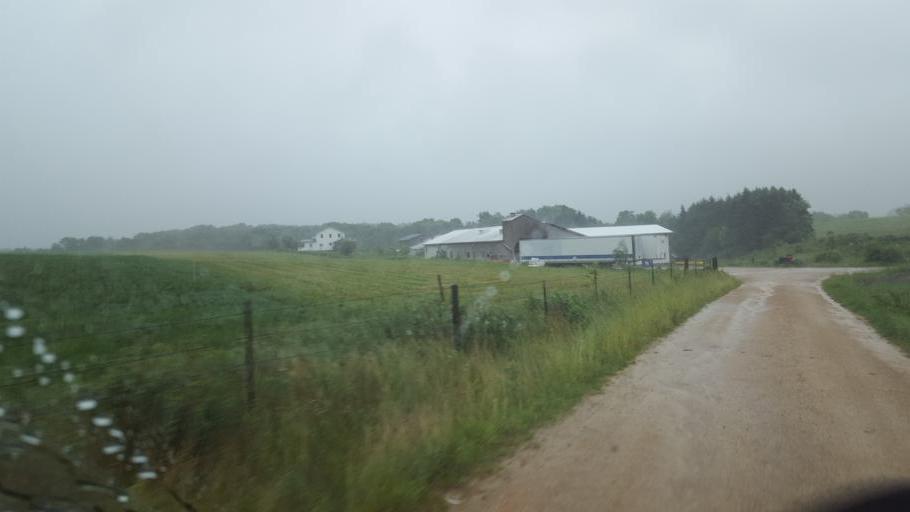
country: US
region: Wisconsin
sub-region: Vernon County
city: Hillsboro
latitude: 43.6213
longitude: -90.4482
